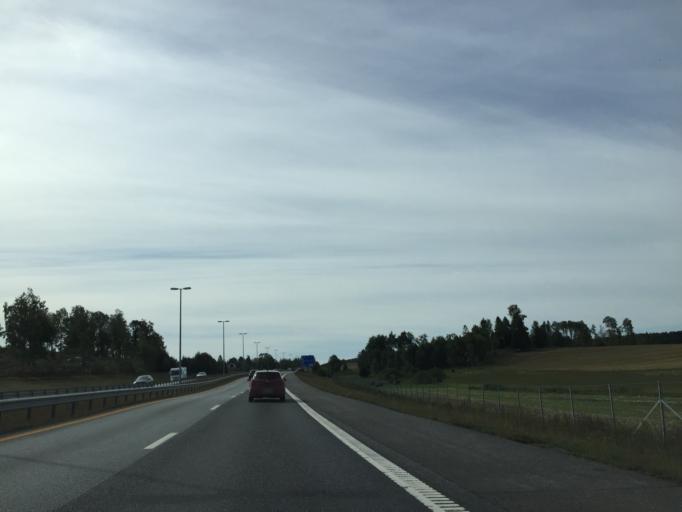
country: NO
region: Akershus
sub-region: Vestby
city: Vestby
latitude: 59.6352
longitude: 10.7384
